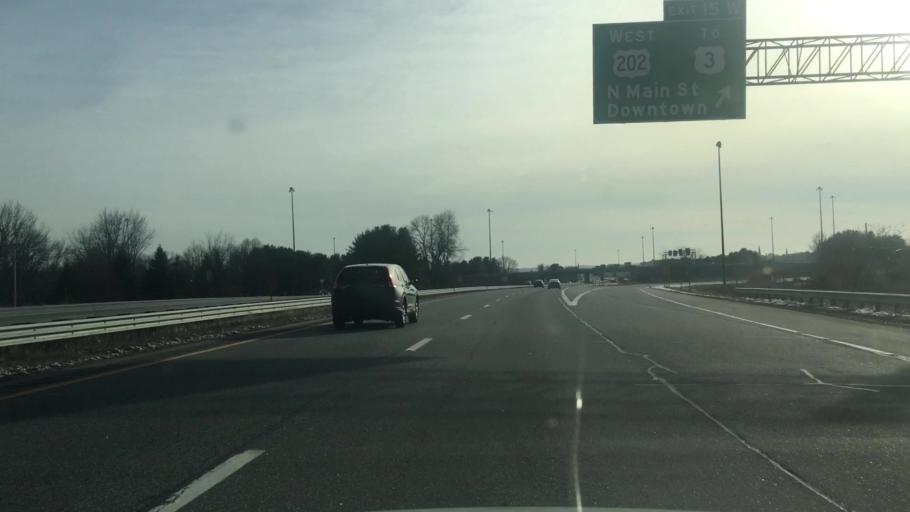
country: US
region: New Hampshire
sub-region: Merrimack County
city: Concord
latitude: 43.2207
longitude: -71.5340
